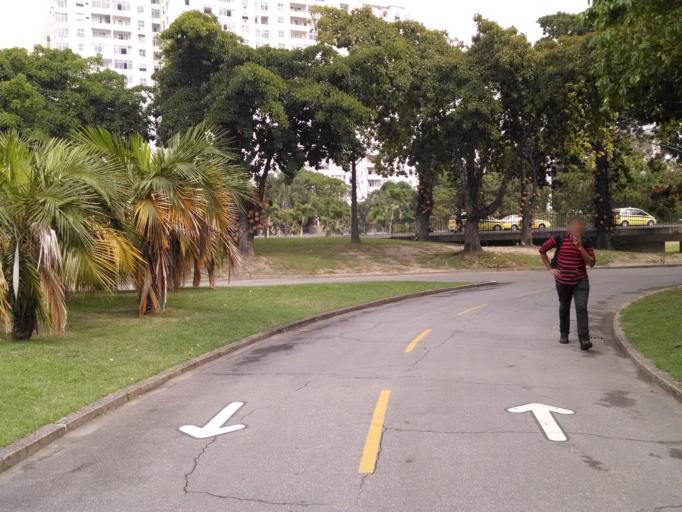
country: BR
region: Rio de Janeiro
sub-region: Rio De Janeiro
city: Rio de Janeiro
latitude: -22.9385
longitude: -43.1697
